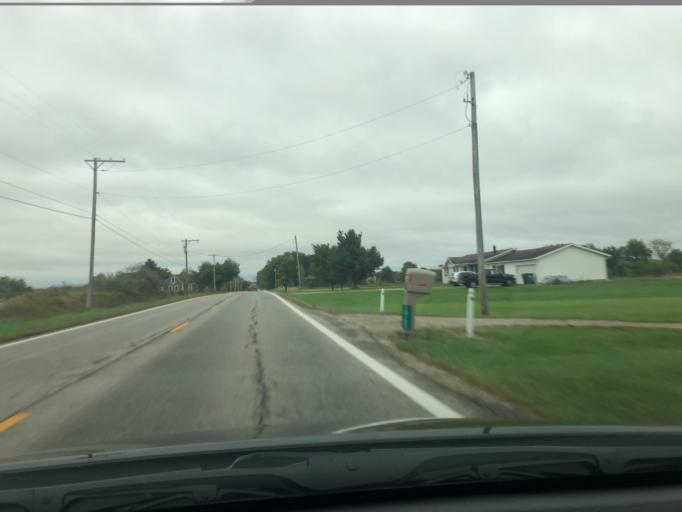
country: US
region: Ohio
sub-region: Union County
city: New California
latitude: 40.2656
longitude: -83.2426
